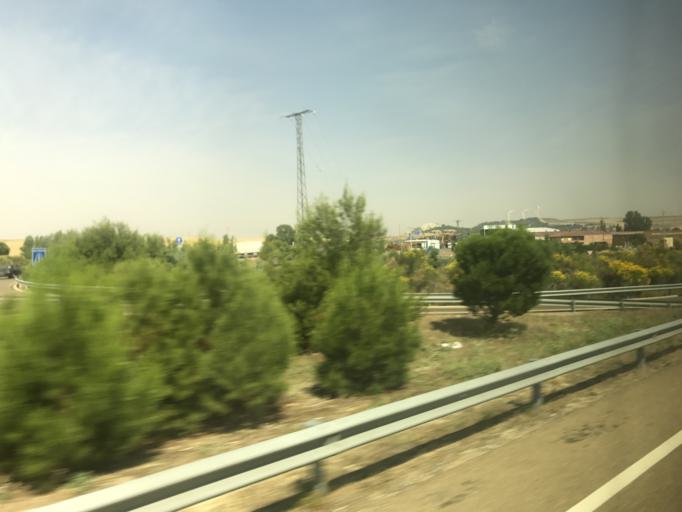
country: ES
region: Castille and Leon
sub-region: Provincia de Palencia
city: Villalobon
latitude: 42.0189
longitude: -4.5070
